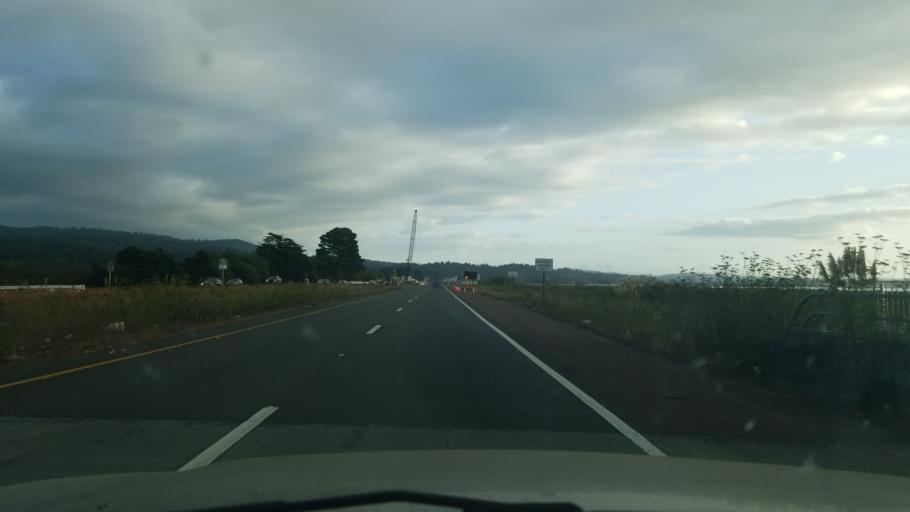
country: US
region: California
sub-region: Humboldt County
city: Bayside
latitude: 40.8464
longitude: -124.0822
